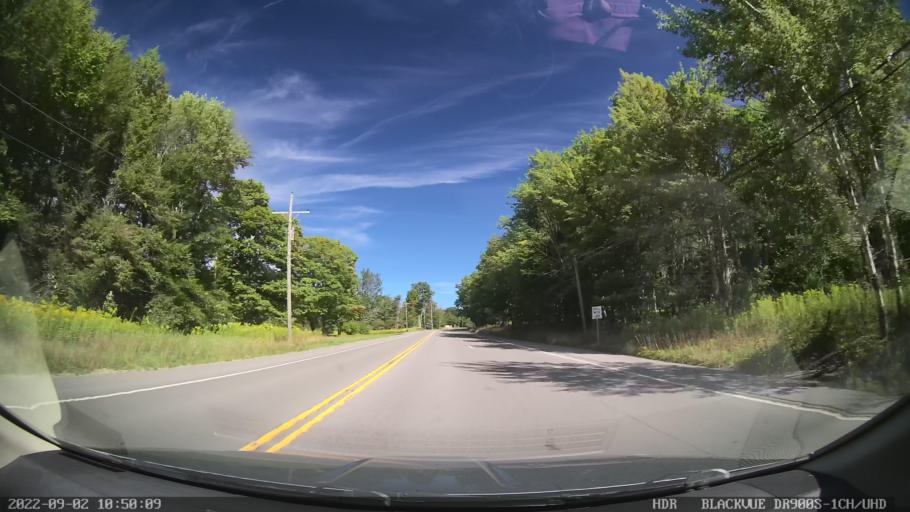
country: US
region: Pennsylvania
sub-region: Tioga County
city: Blossburg
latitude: 41.6100
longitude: -77.1167
